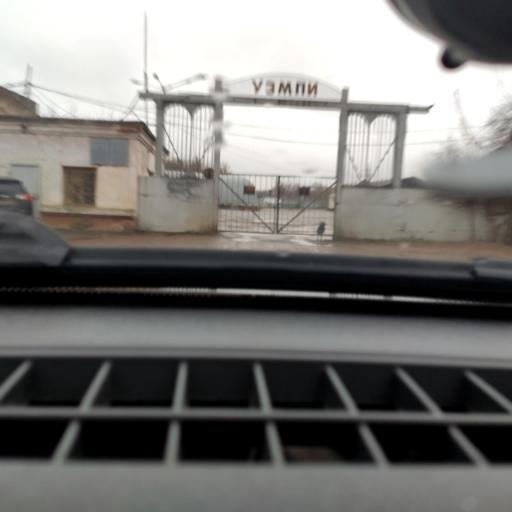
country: RU
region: Bashkortostan
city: Ufa
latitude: 54.7976
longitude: 56.0822
